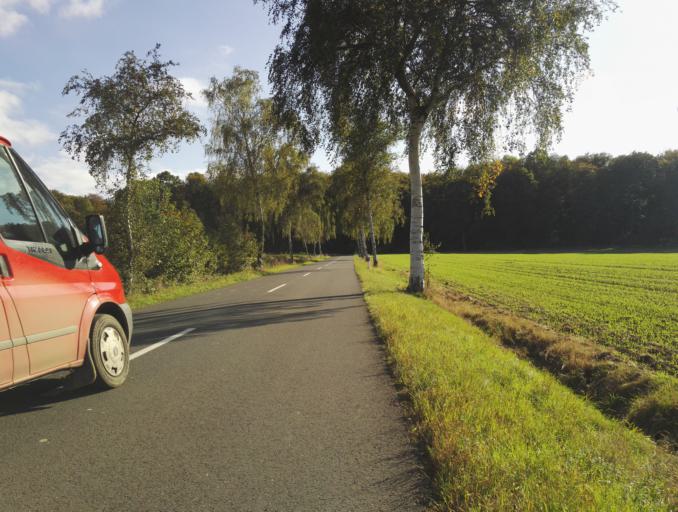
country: DE
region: Lower Saxony
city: Holle
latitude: 52.1388
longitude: 10.1367
